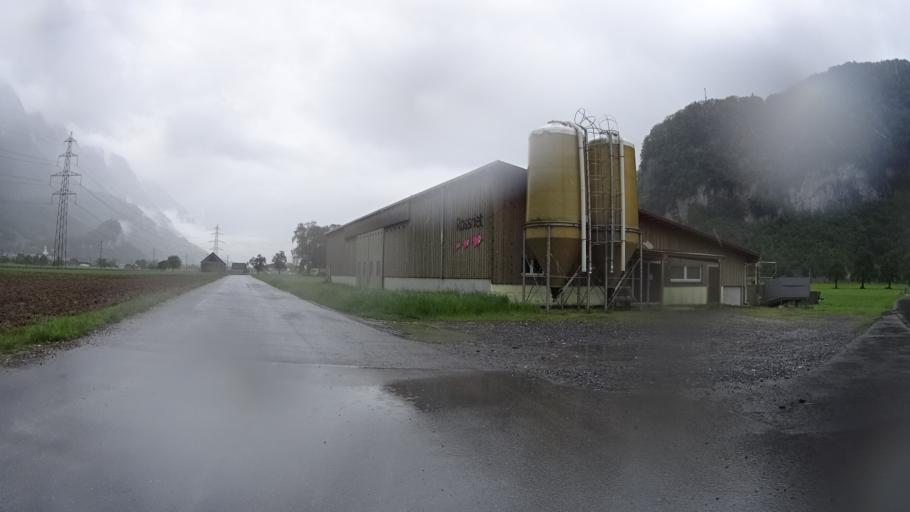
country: CH
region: Saint Gallen
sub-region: Wahlkreis Sarganserland
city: Walenstadt
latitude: 47.1093
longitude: 9.3290
